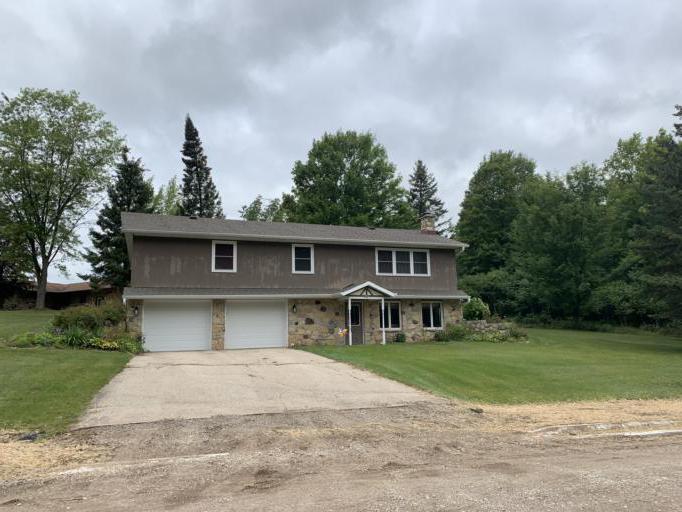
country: US
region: Wisconsin
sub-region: Oconto County
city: Oconto Falls
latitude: 45.0673
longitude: -88.0259
